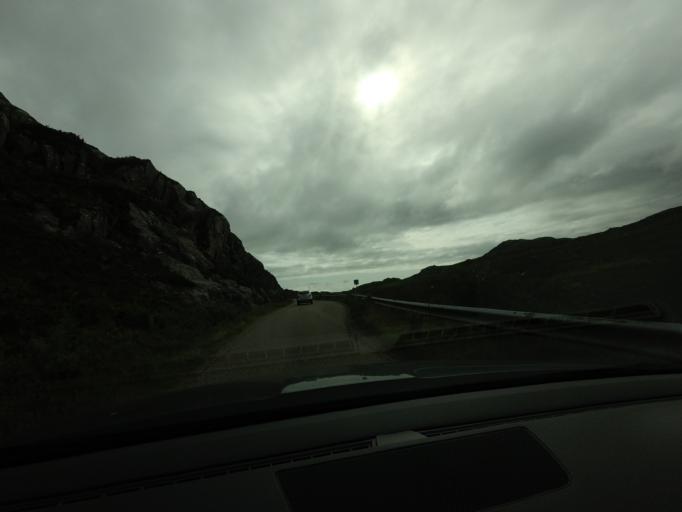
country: GB
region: Scotland
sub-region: Highland
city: Ullapool
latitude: 58.4347
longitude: -4.9678
